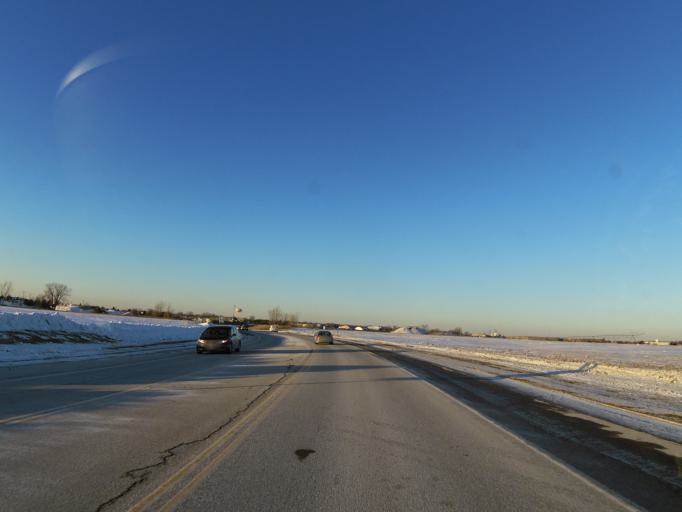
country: US
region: Minnesota
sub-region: Dakota County
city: Rosemount
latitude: 44.7190
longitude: -93.1296
